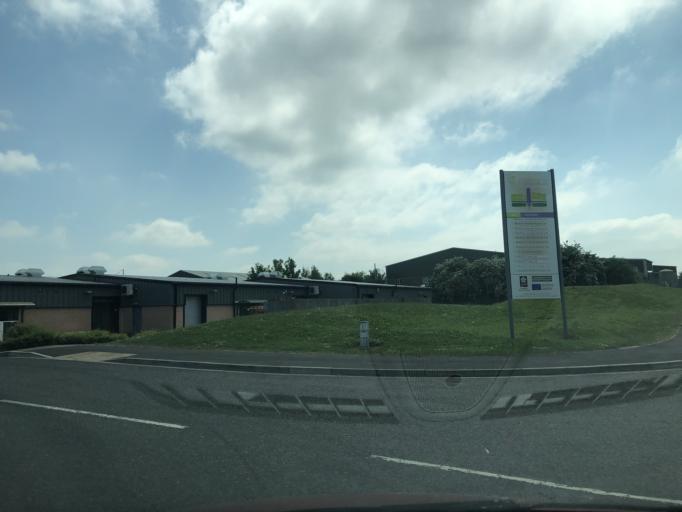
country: GB
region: England
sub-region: North Yorkshire
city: Bedale
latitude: 54.3082
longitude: -1.5670
